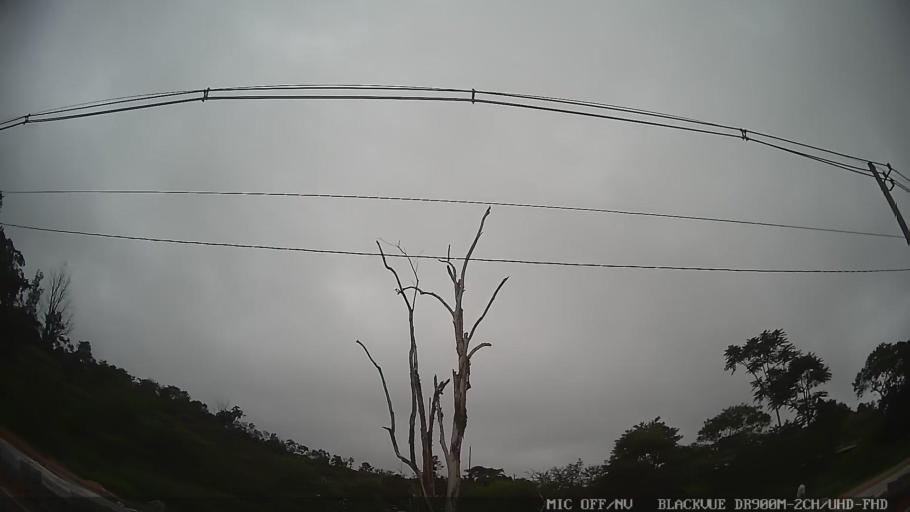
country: BR
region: Sao Paulo
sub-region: Embu
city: Embu
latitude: -23.6462
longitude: -46.8325
